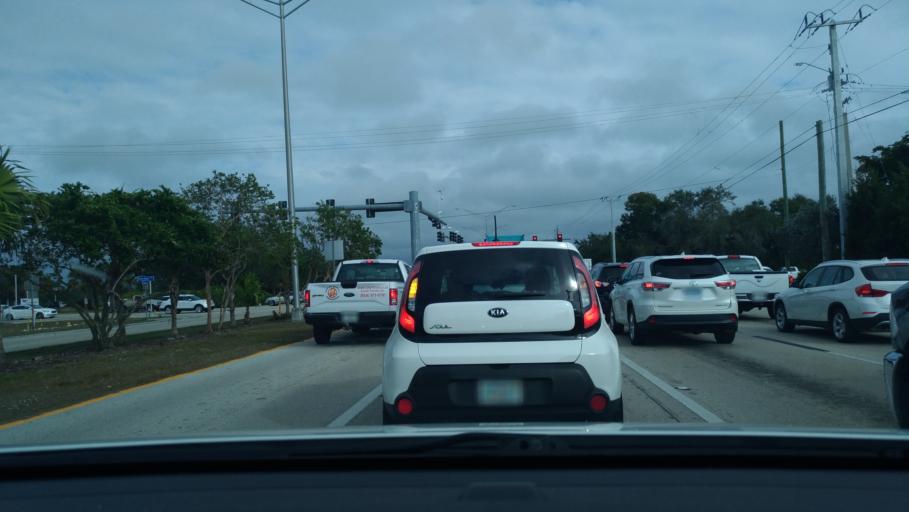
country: US
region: Florida
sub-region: Lee County
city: Estero
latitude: 26.4313
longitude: -81.7892
